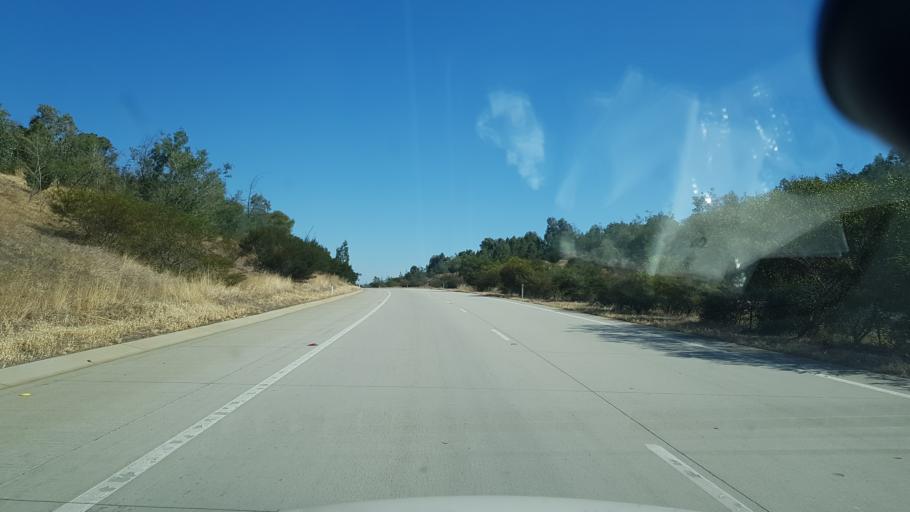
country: AU
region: New South Wales
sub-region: Albury Municipality
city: Lavington
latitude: -35.9176
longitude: 147.0987
